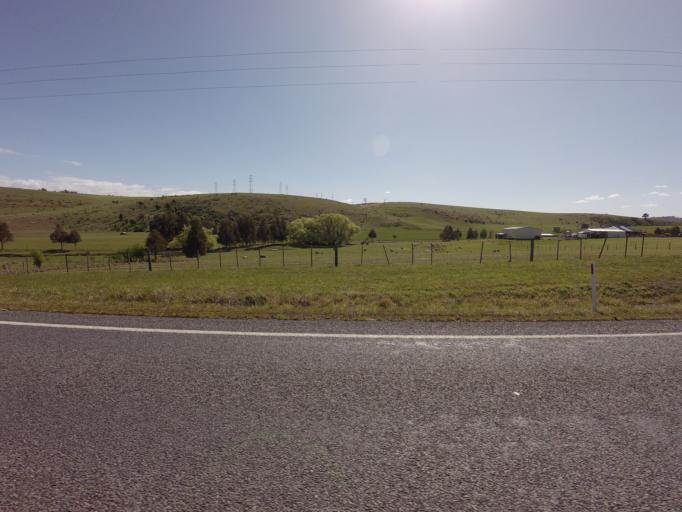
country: AU
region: Tasmania
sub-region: Derwent Valley
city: New Norfolk
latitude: -42.6612
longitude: 146.9349
